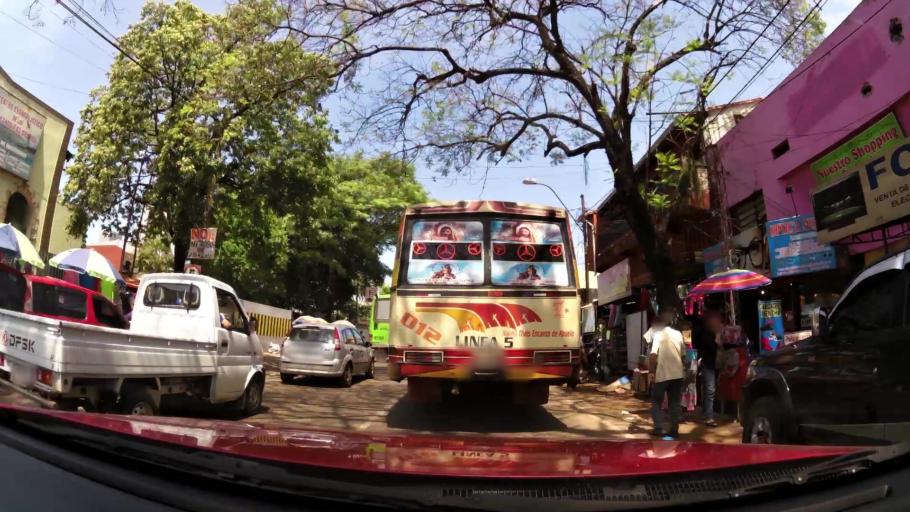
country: PY
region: Central
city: San Lorenzo
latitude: -25.3439
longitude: -57.5085
